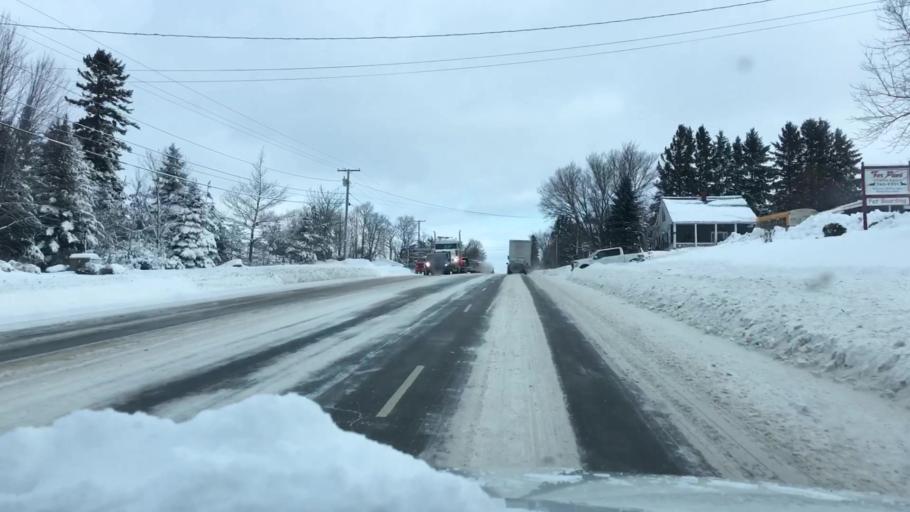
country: US
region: Maine
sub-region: Aroostook County
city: Presque Isle
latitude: 46.7246
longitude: -68.0047
